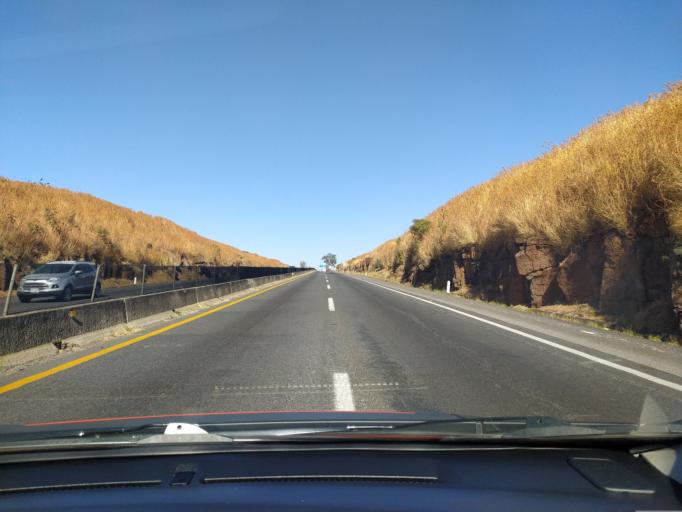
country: MX
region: Jalisco
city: Tepatitlan de Morelos
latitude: 20.8089
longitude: -102.8085
